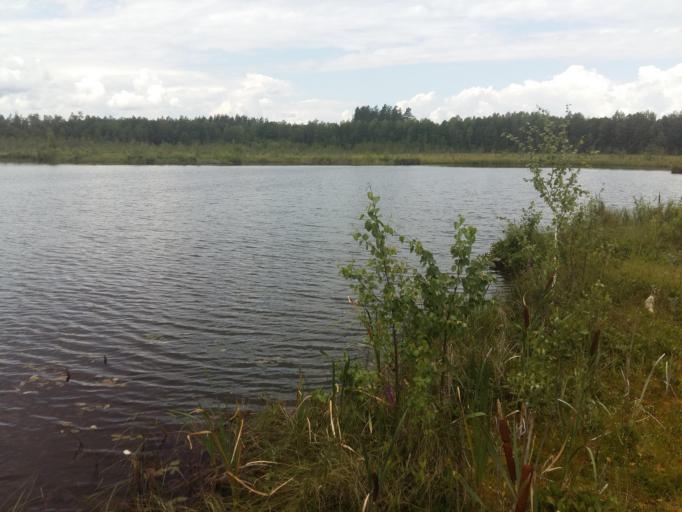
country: LT
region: Alytaus apskritis
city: Druskininkai
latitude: 54.0377
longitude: 24.2783
